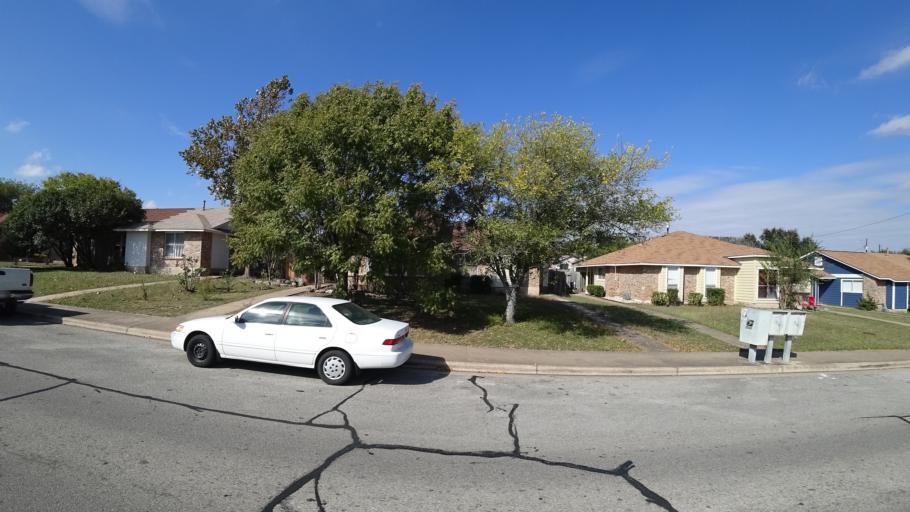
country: US
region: Texas
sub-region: Travis County
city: Windemere
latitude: 30.4506
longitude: -97.6465
